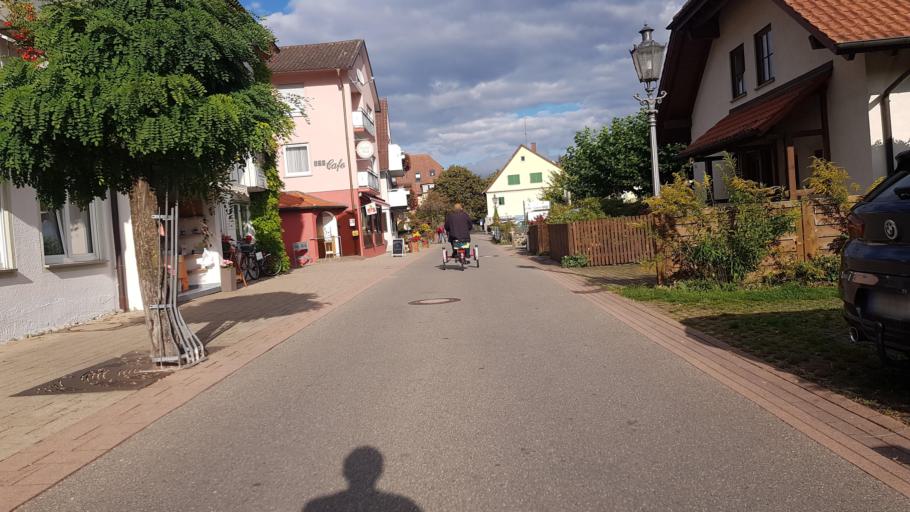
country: DE
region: Baden-Wuerttemberg
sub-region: Tuebingen Region
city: Immenstaad am Bodensee
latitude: 47.6637
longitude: 9.3647
